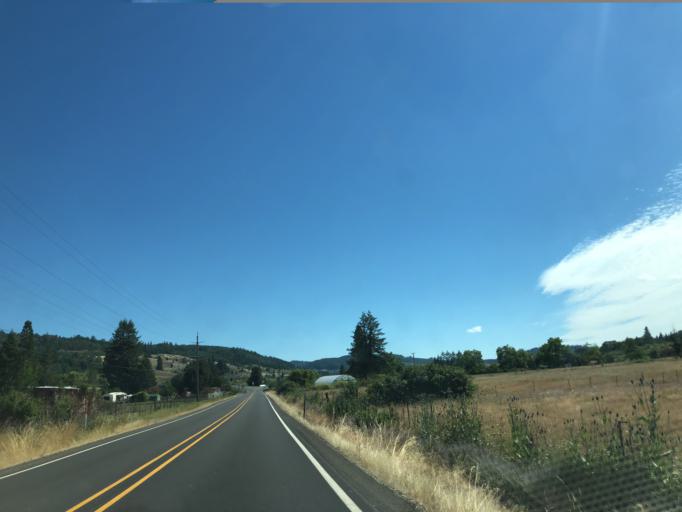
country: US
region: Oregon
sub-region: Douglas County
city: Yoncalla
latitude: 43.5683
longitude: -123.2809
